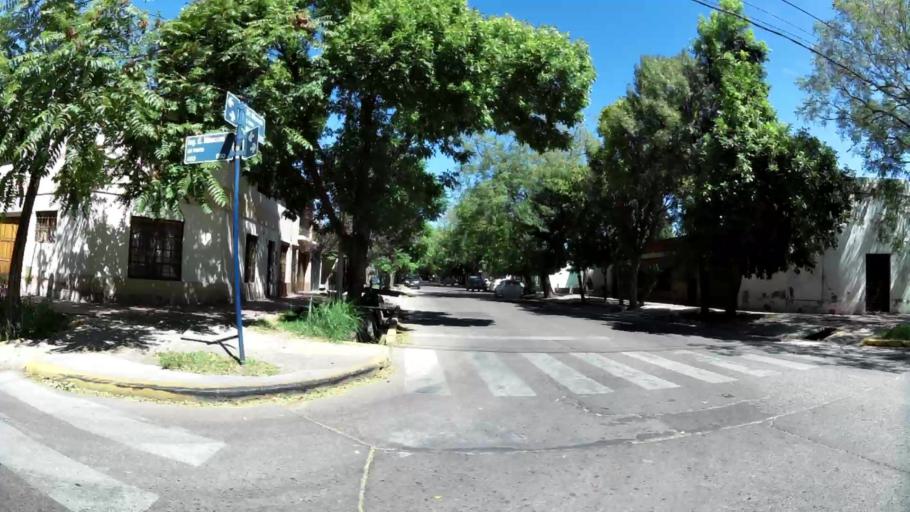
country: AR
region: Mendoza
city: Las Heras
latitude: -32.8625
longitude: -68.8402
